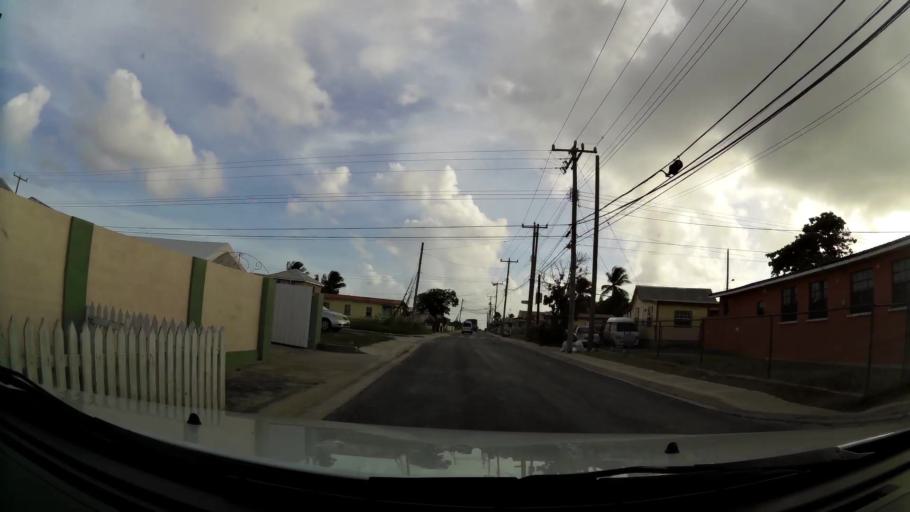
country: BB
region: Christ Church
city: Oistins
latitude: 13.0543
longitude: -59.5192
